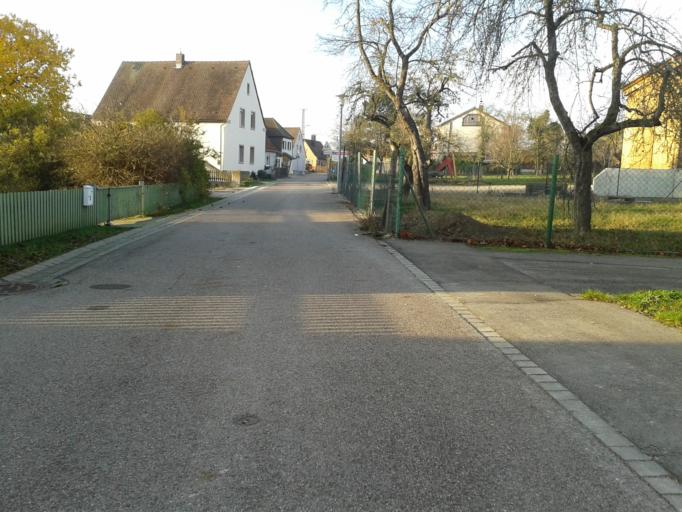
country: DE
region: Bavaria
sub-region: Regierungsbezirk Mittelfranken
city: Gallmersgarten
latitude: 49.4526
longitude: 10.2760
